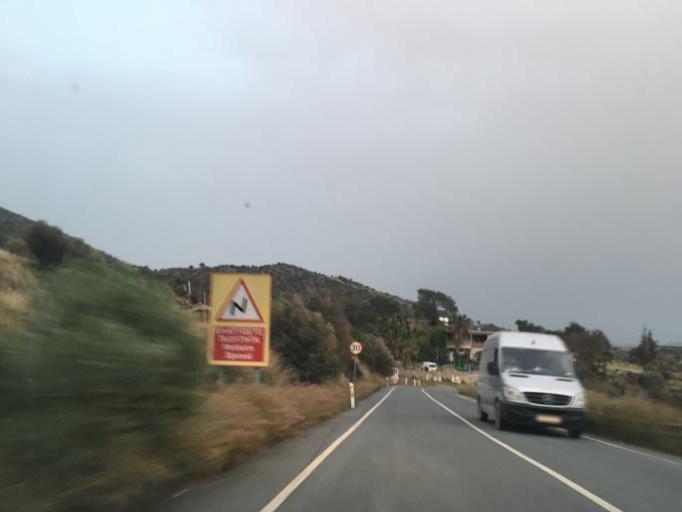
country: CY
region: Limassol
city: Parekklisha
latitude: 34.7866
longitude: 33.1637
